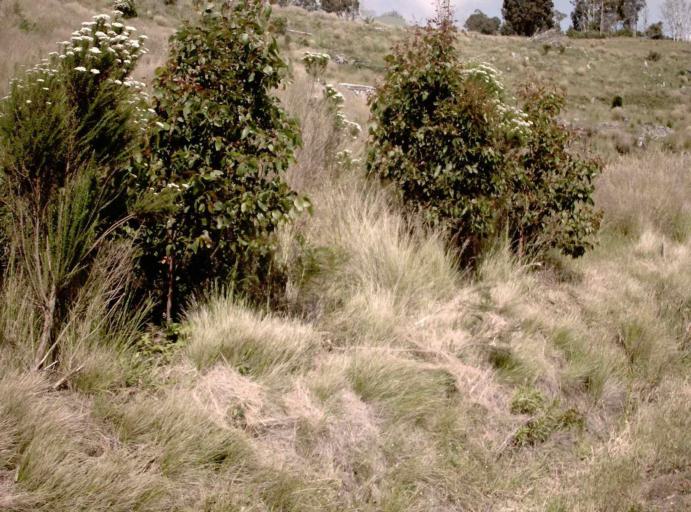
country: AU
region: Victoria
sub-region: Latrobe
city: Traralgon
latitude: -38.3542
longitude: 146.5691
